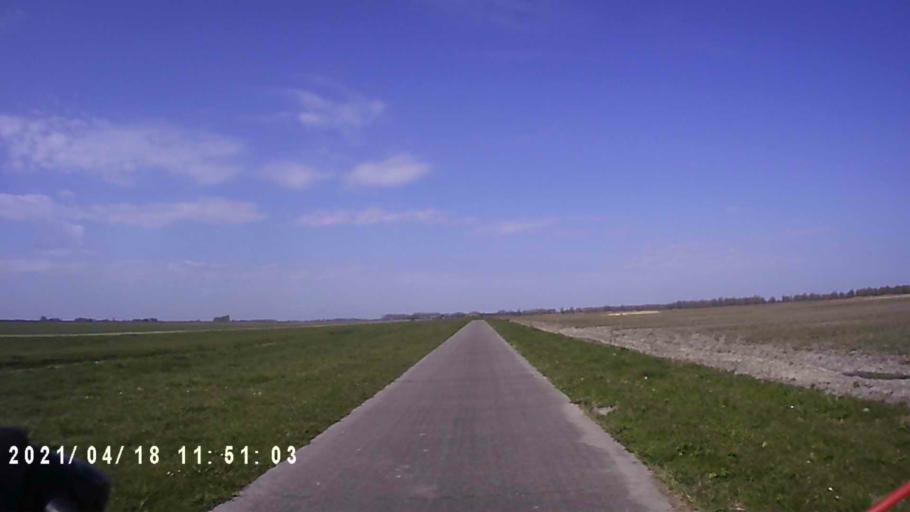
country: NL
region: Friesland
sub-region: Gemeente Kollumerland en Nieuwkruisland
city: Kollum
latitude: 53.3217
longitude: 6.2266
